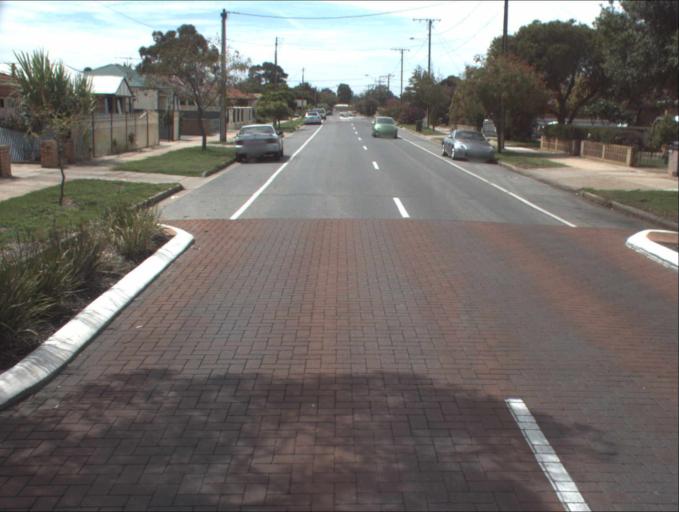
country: AU
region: South Australia
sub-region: Port Adelaide Enfield
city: Alberton
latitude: -34.8458
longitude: 138.5341
